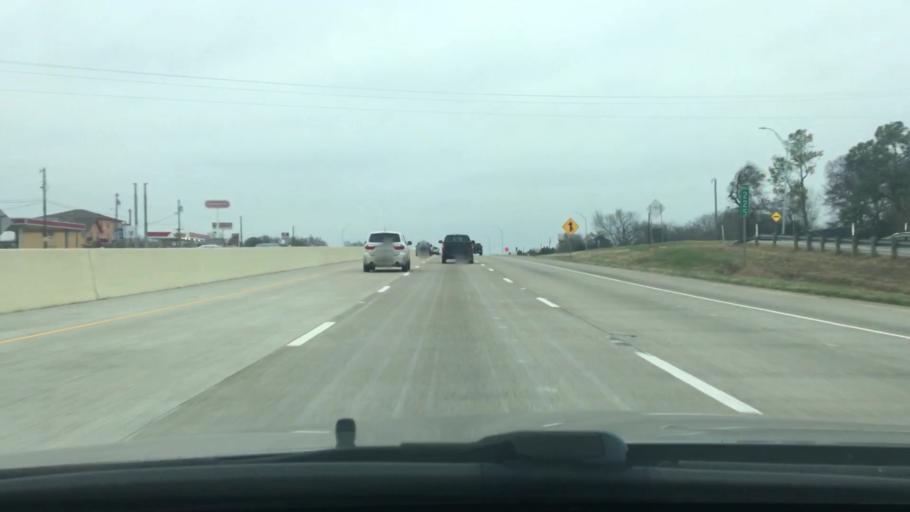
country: US
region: Texas
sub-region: Navarro County
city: Corsicana
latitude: 32.0085
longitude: -96.4340
